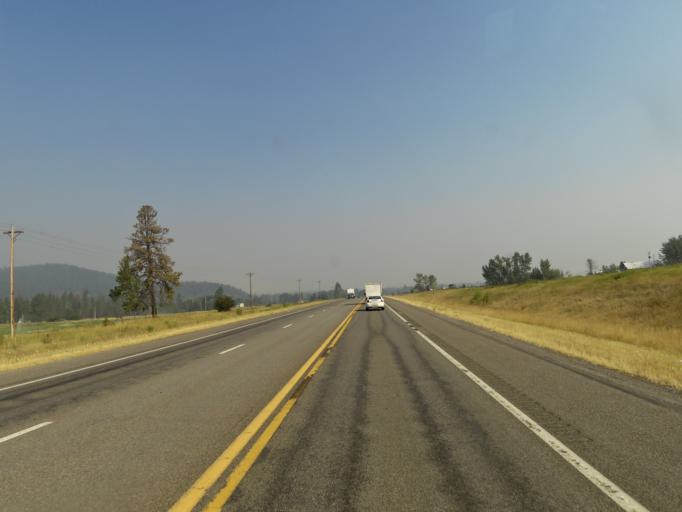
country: US
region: Montana
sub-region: Missoula County
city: Frenchtown
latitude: 47.1031
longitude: -114.0442
